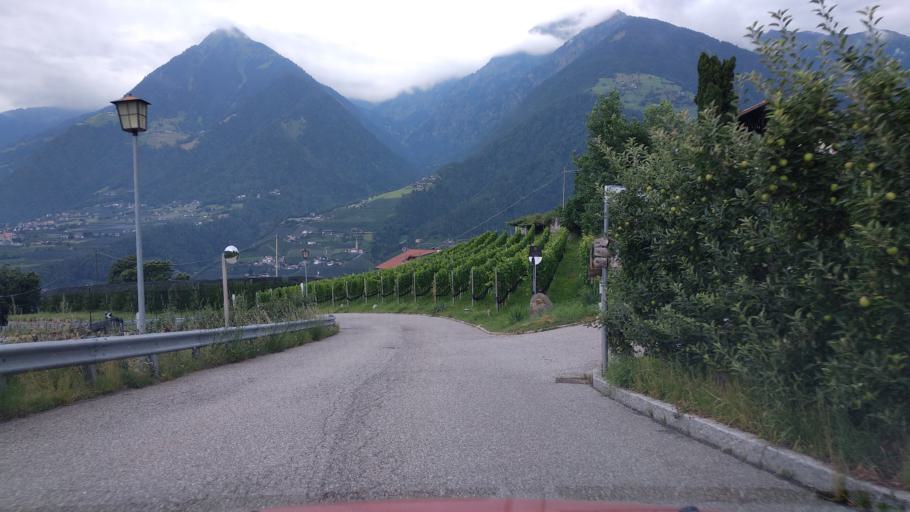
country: IT
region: Trentino-Alto Adige
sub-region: Bolzano
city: Scena
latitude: 46.6894
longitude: 11.1938
